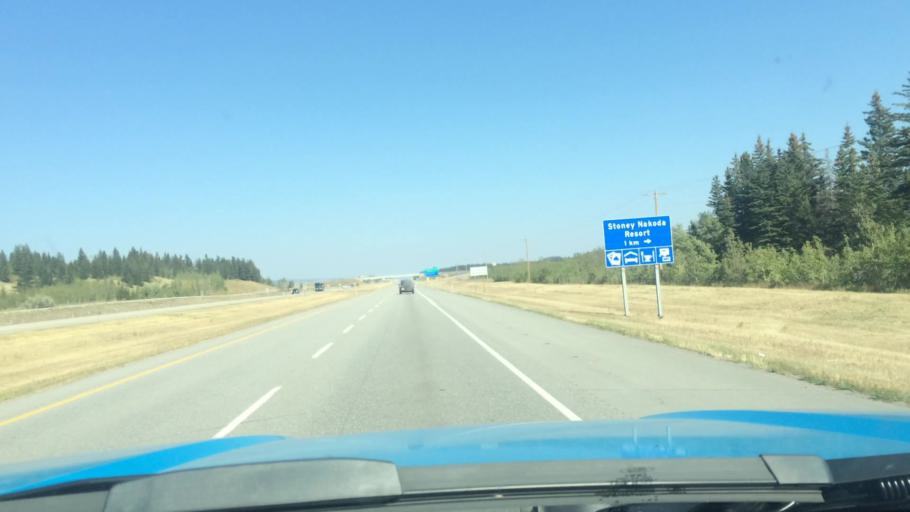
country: CA
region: Alberta
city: Canmore
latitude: 51.0989
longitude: -115.0325
